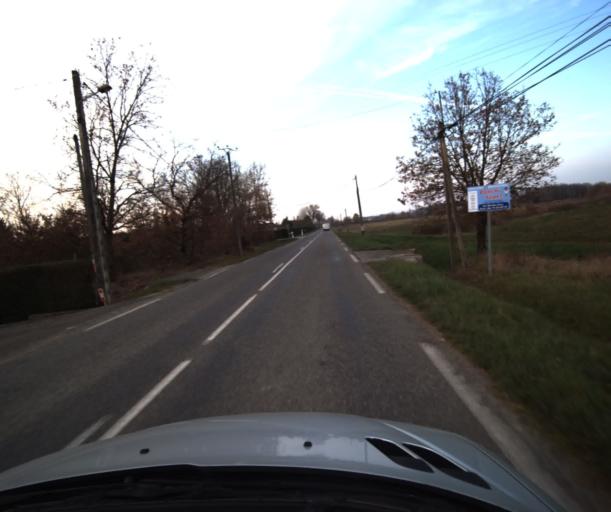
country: FR
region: Midi-Pyrenees
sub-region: Departement de la Haute-Garonne
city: Fronton
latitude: 43.8633
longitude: 1.3826
